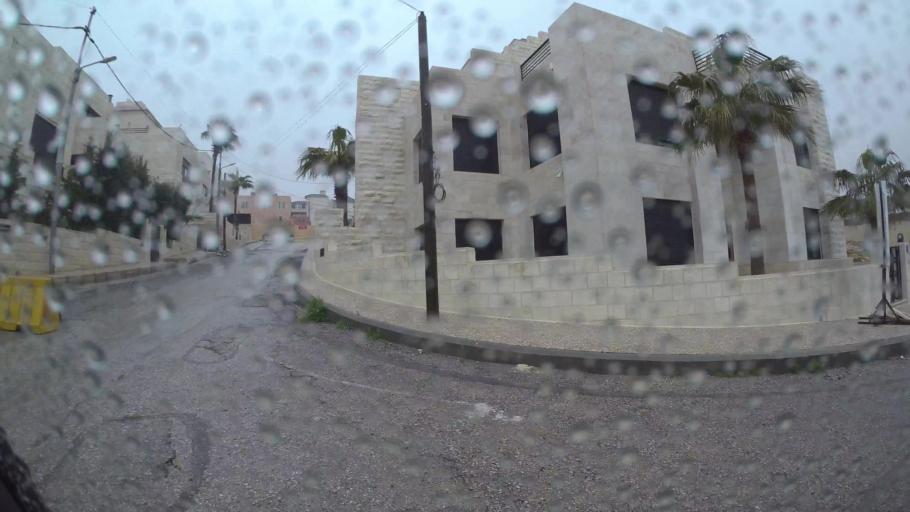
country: JO
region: Amman
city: Al Jubayhah
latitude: 32.0079
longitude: 35.8307
